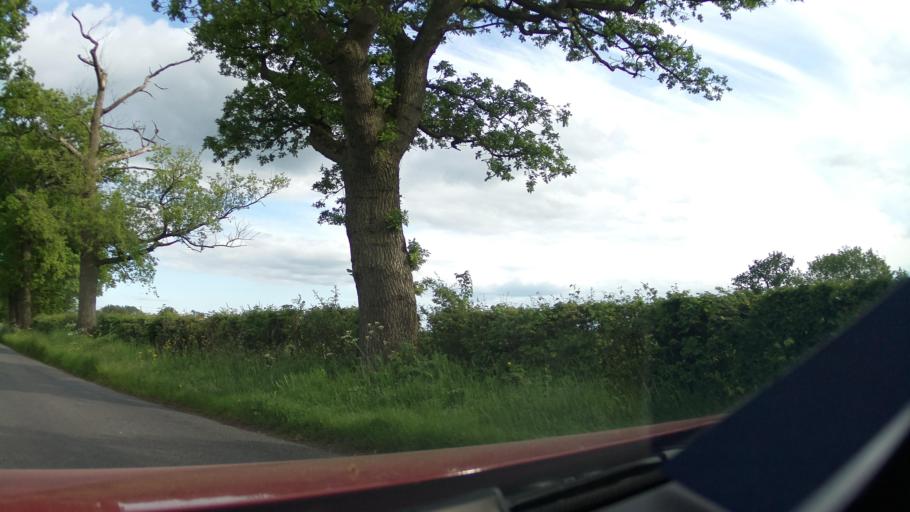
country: GB
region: England
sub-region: Gloucestershire
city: Moreton in Marsh
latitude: 51.9981
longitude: -1.7106
